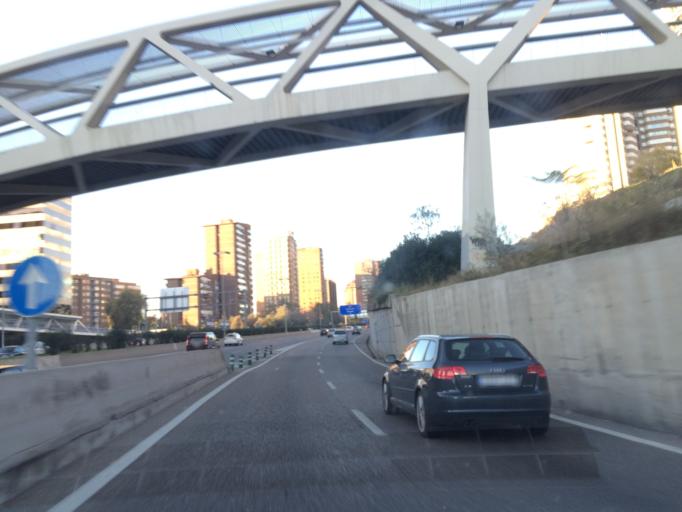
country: ES
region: Madrid
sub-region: Provincia de Madrid
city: Pinar de Chamartin
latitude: 40.4748
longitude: -3.6737
